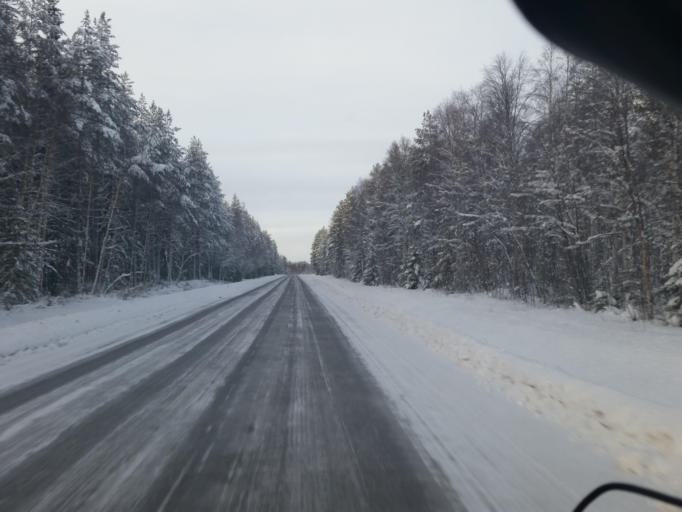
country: SE
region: Norrbotten
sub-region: Pitea Kommun
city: Norrfjarden
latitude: 65.4353
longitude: 21.4806
